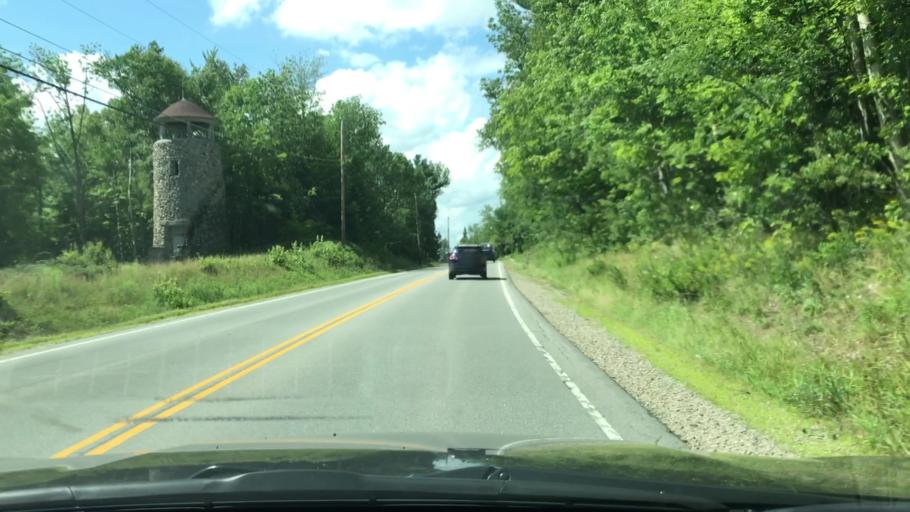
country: US
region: New Hampshire
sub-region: Coos County
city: Jefferson
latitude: 44.3716
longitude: -71.4069
